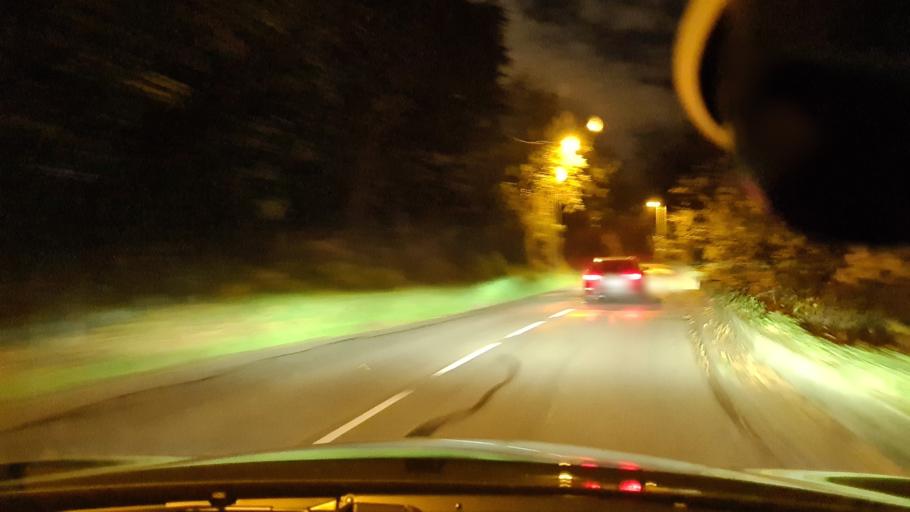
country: FR
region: Rhone-Alpes
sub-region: Departement du Rhone
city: Limonest
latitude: 45.8279
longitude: 4.7866
